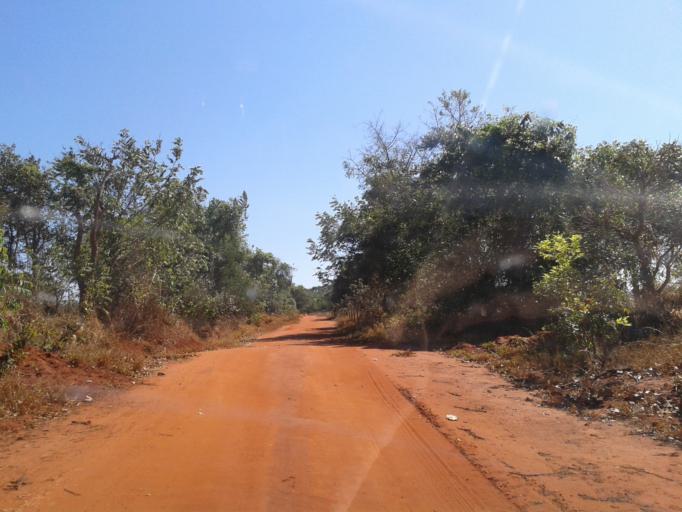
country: BR
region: Minas Gerais
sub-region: Monte Alegre De Minas
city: Monte Alegre de Minas
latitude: -18.8712
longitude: -49.1317
